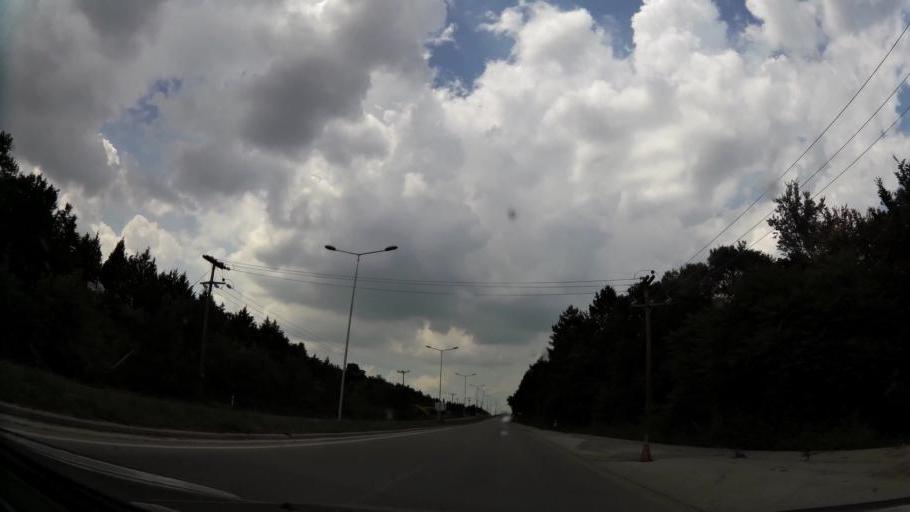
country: GR
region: West Macedonia
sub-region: Nomos Kozanis
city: Koila
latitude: 40.3233
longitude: 21.8277
